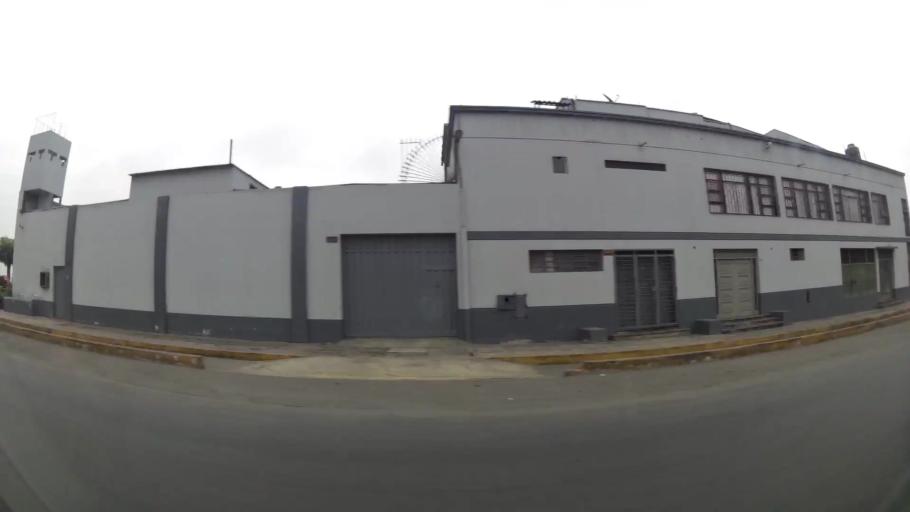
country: PE
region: Lima
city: Lima
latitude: -12.0475
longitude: -77.0530
